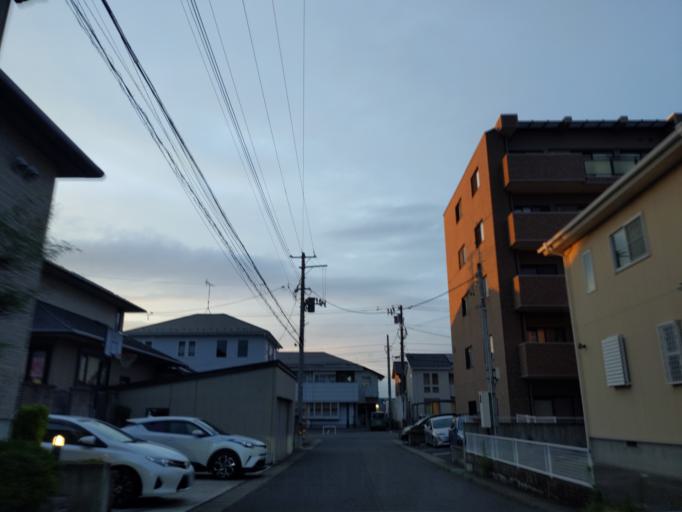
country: JP
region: Fukushima
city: Koriyama
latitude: 37.4103
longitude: 140.3546
